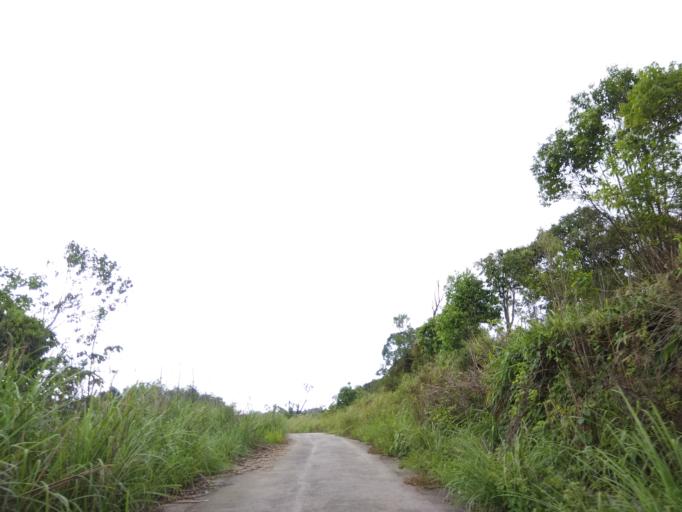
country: BD
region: Chittagong
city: Bandarban
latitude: 21.7404
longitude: 92.4205
